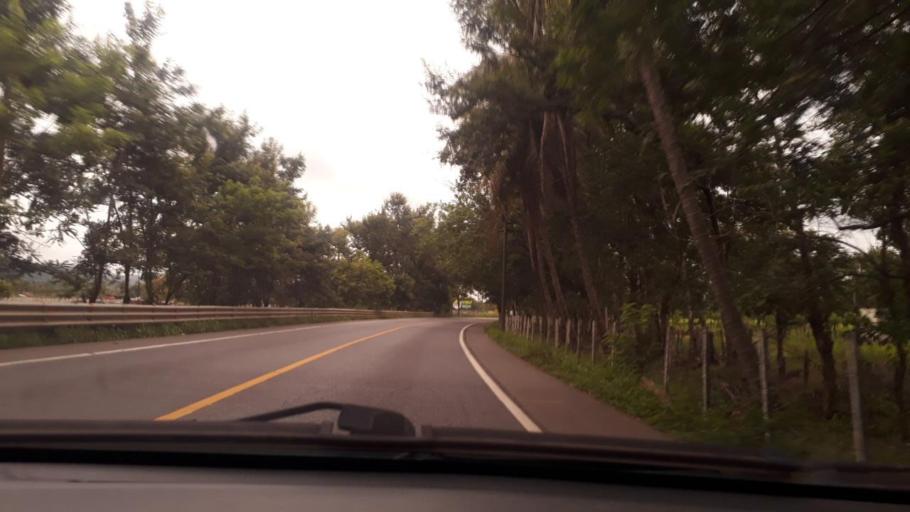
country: GT
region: Izabal
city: Morales
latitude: 15.4807
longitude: -88.8815
